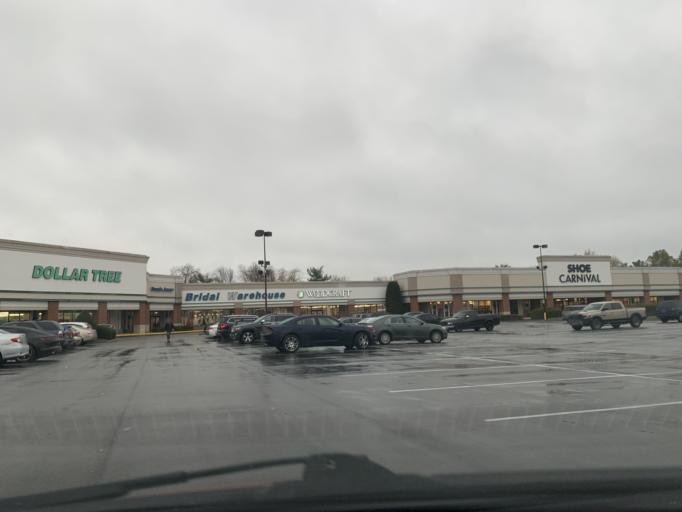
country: US
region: Kentucky
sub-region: Jefferson County
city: Hurstbourne Acres
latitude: 38.2204
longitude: -85.5845
